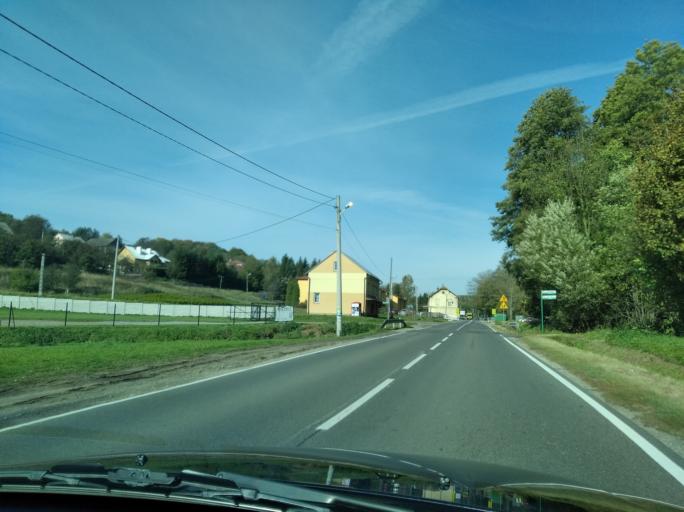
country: PL
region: Subcarpathian Voivodeship
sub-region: Powiat strzyzowski
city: Wisniowa
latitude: 49.9023
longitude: 21.6326
